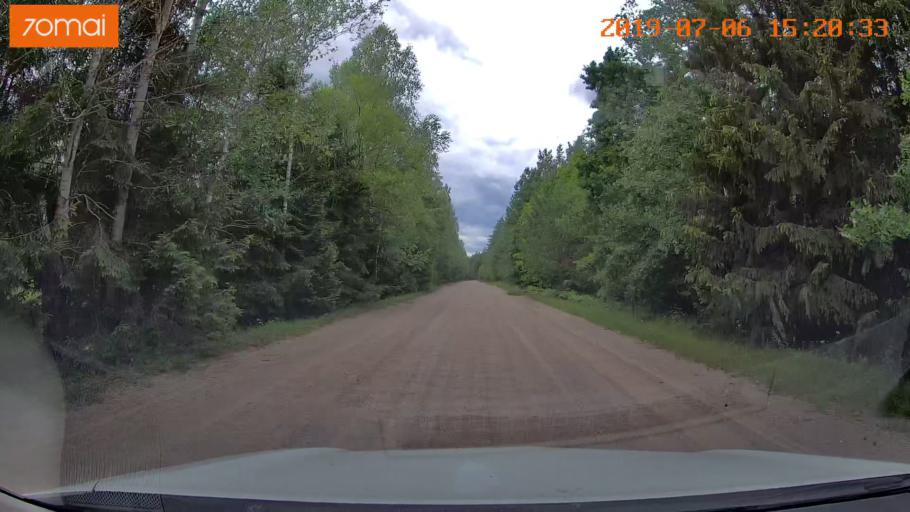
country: BY
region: Minsk
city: Valozhyn
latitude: 54.0069
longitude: 26.6329
